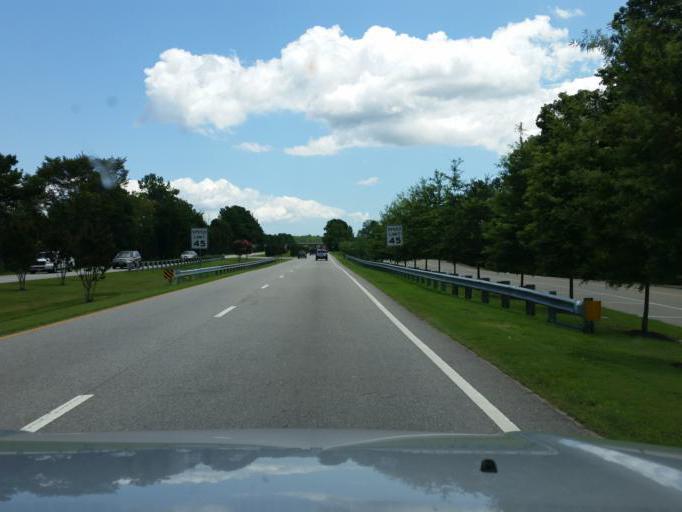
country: US
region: Virginia
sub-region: City of Williamsburg
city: Williamsburg
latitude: 37.2390
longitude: -76.6460
